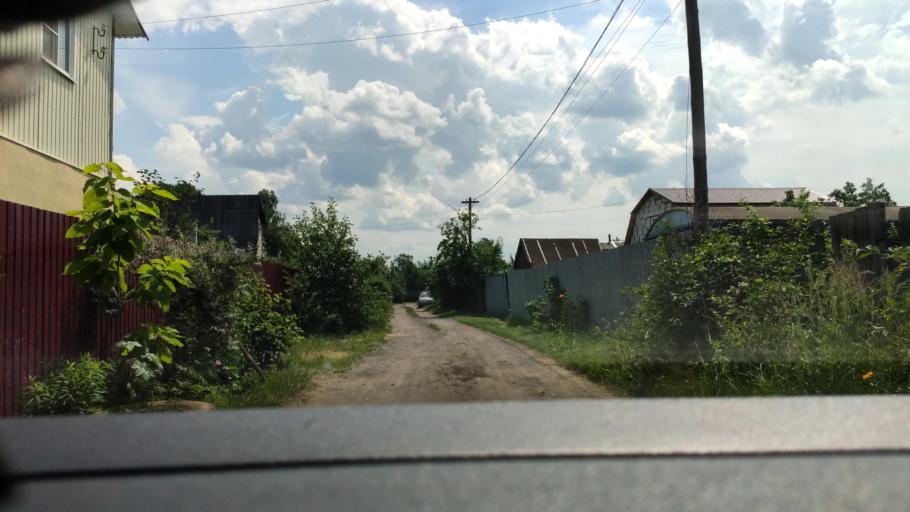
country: RU
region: Voronezj
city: Maslovka
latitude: 51.6093
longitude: 39.2874
